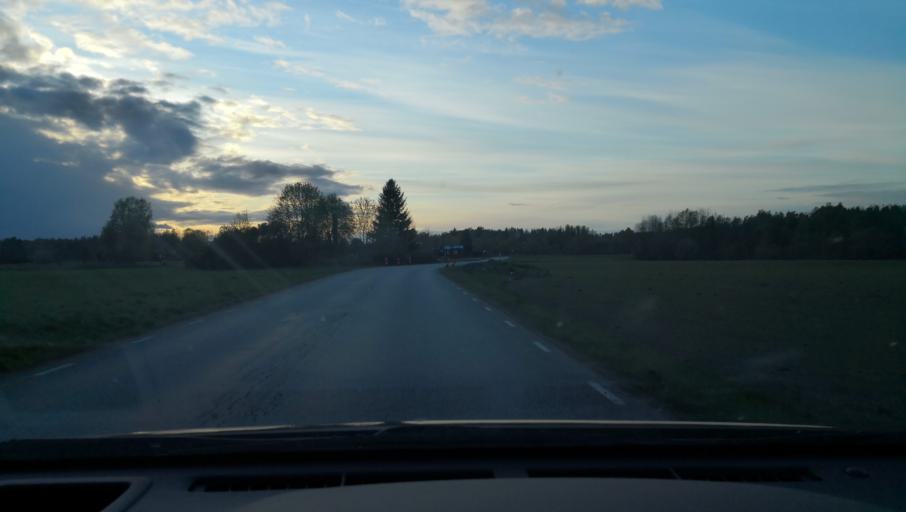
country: SE
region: OErebro
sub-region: Askersunds Kommun
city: Asbro
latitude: 58.9275
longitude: 15.0327
